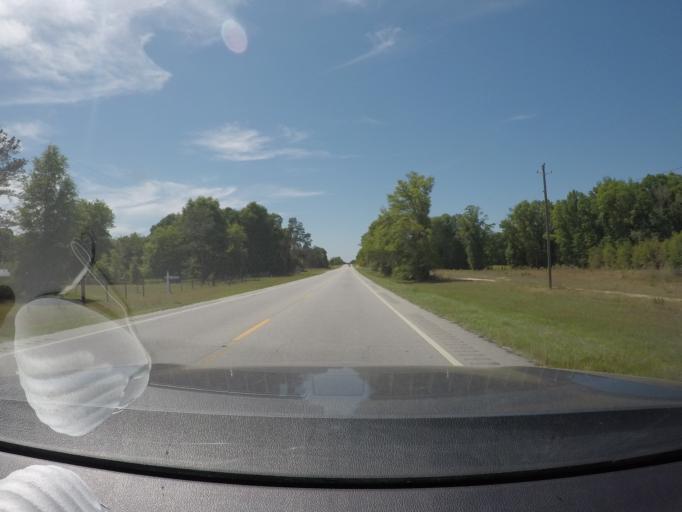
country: US
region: Georgia
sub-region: Bryan County
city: Pembroke
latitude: 32.1460
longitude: -81.7596
